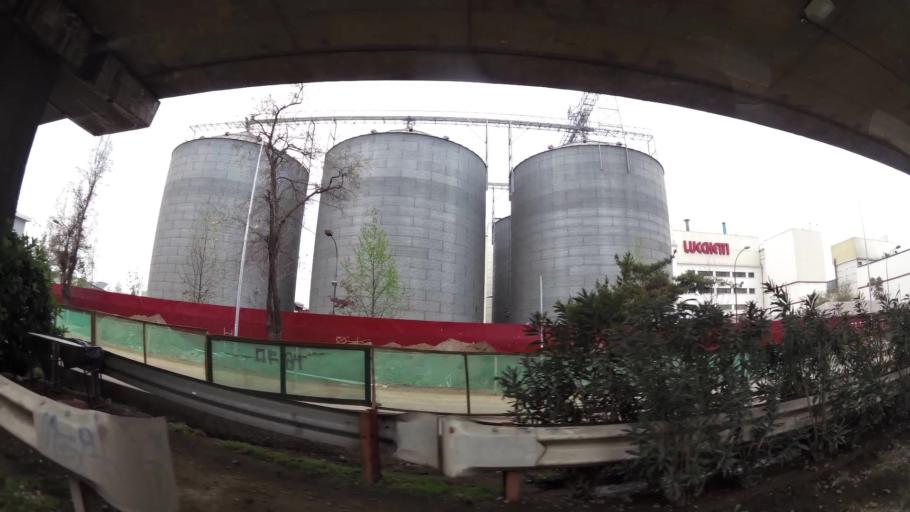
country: CL
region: Santiago Metropolitan
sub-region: Provincia de Santiago
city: Santiago
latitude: -33.4764
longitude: -70.6227
